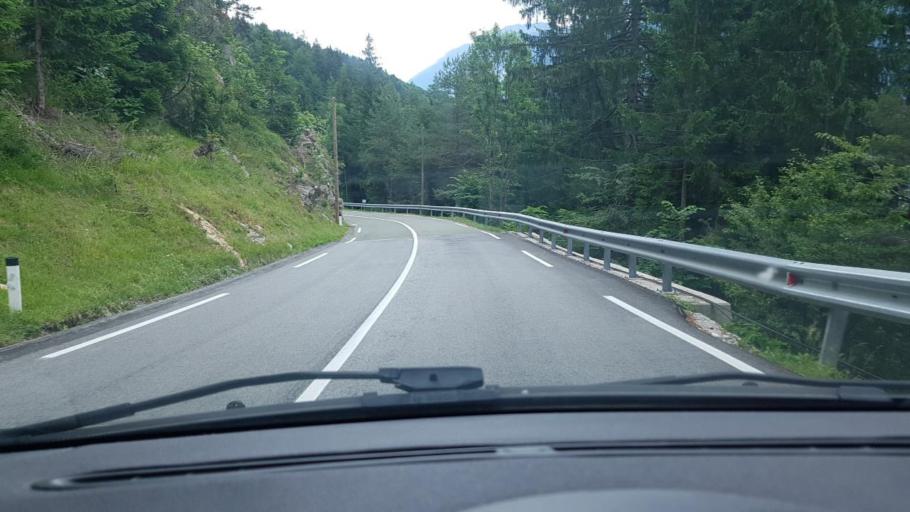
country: SI
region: Kranjska Gora
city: Kranjska Gora
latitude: 46.4985
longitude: 13.7588
